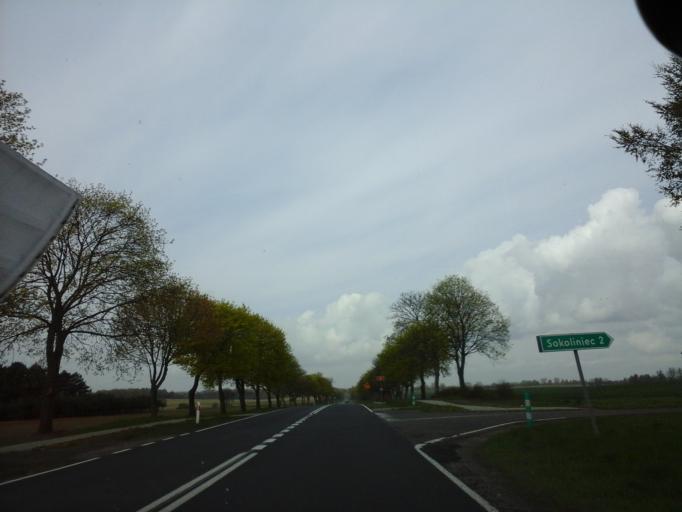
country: PL
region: West Pomeranian Voivodeship
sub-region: Powiat choszczenski
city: Recz
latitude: 53.2694
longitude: 15.4967
